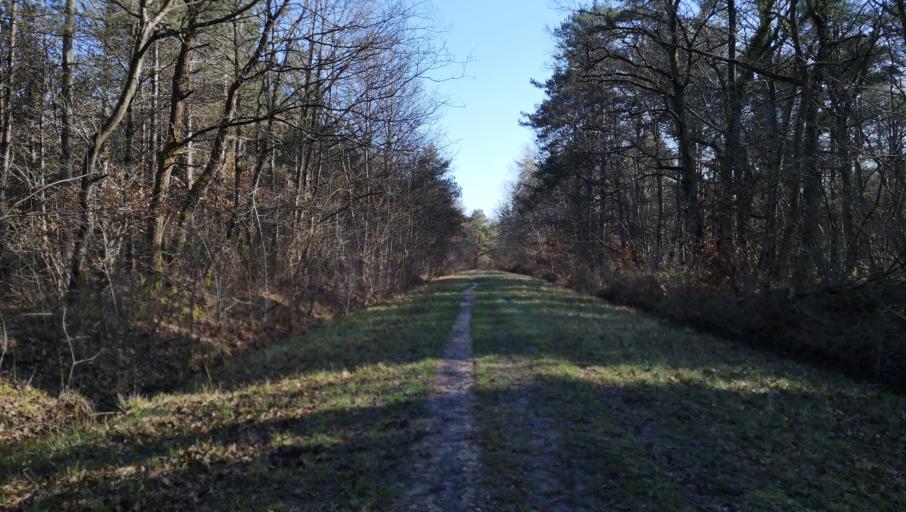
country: FR
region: Centre
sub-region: Departement du Loiret
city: Chanteau
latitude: 47.9557
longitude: 1.9700
